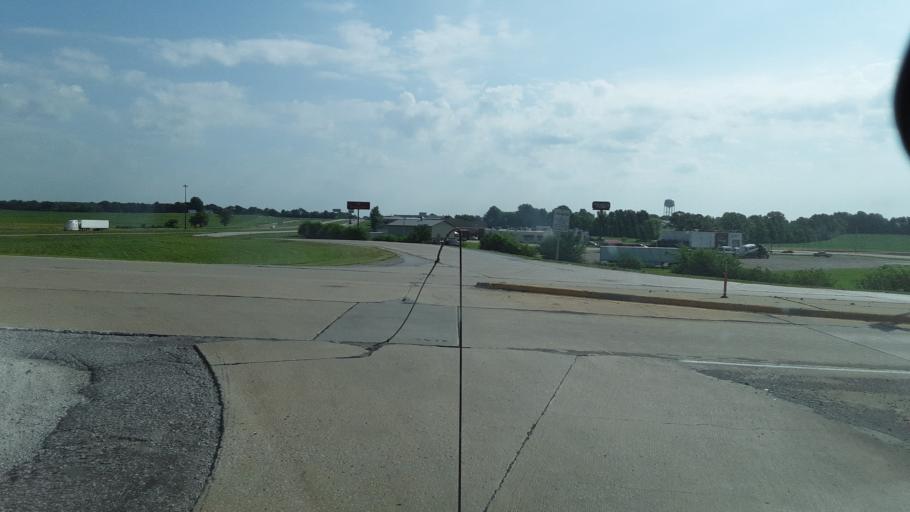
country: US
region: Illinois
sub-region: Fayette County
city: Vandalia
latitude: 38.9682
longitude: -89.1321
